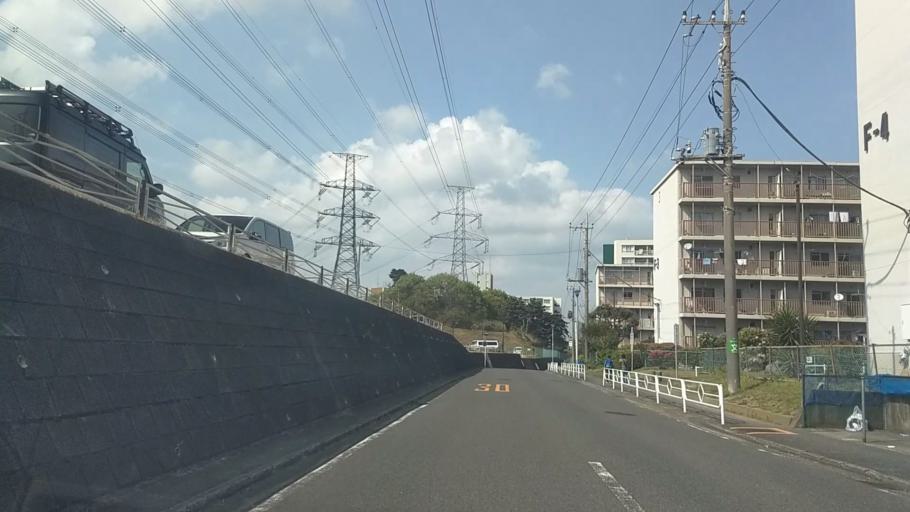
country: JP
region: Kanagawa
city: Kamakura
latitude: 35.3838
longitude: 139.5682
